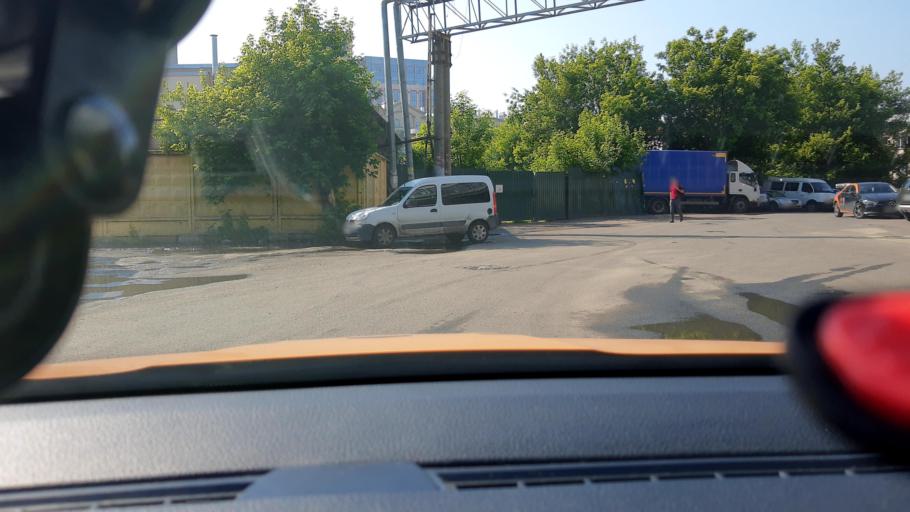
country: RU
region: Moscow
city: Sokol'niki
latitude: 55.7796
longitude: 37.6594
